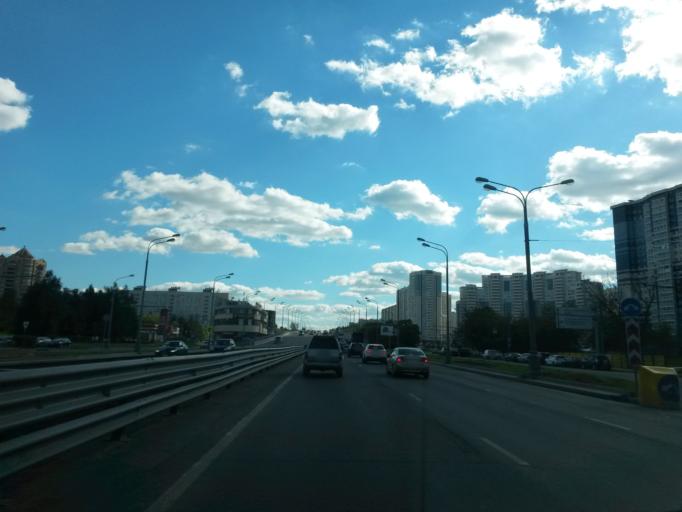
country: RU
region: Moscow
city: Chertanovo Yuzhnoye
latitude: 55.5982
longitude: 37.6034
